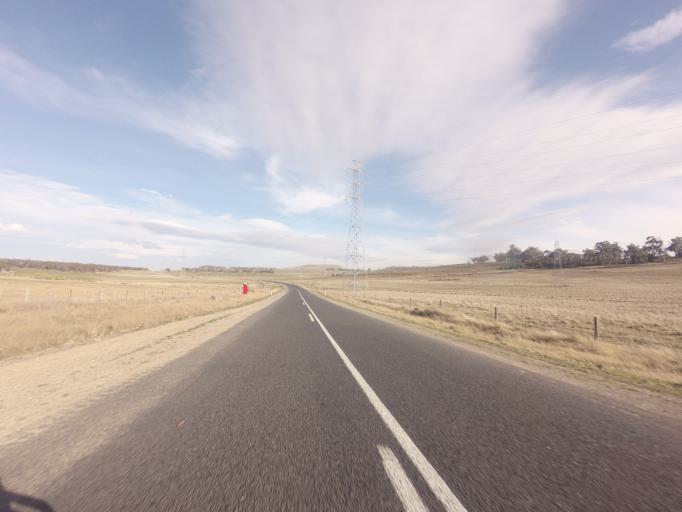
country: AU
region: Tasmania
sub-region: Derwent Valley
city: New Norfolk
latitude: -42.2600
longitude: 146.9377
